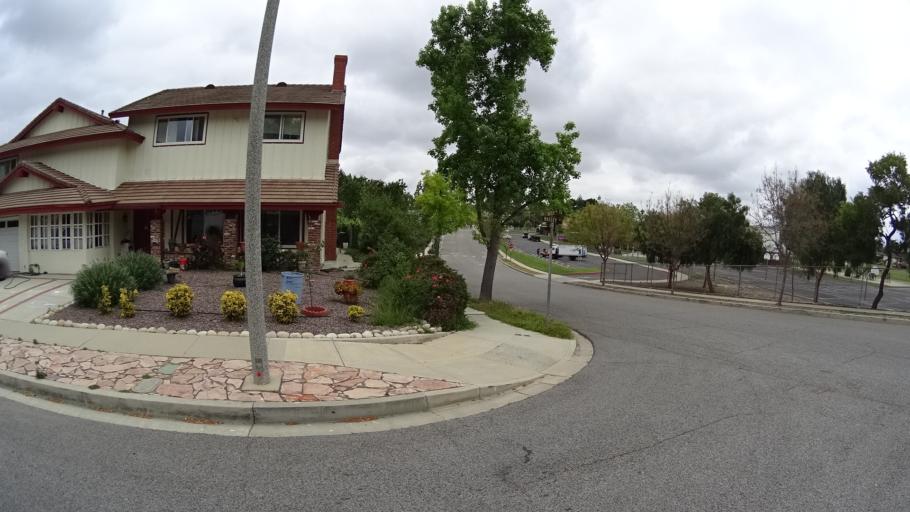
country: US
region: California
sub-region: Ventura County
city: Thousand Oaks
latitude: 34.2017
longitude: -118.8842
